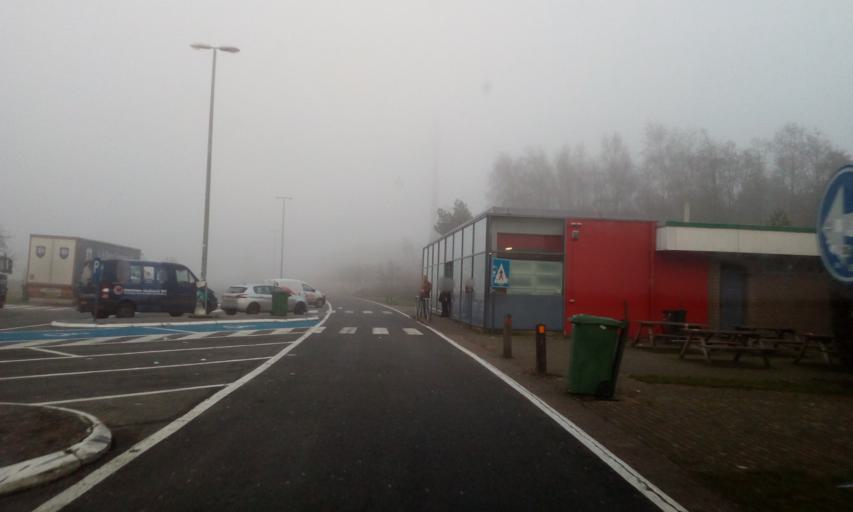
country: BE
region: Flanders
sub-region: Provincie Antwerpen
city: Brecht
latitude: 51.3219
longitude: 4.5861
